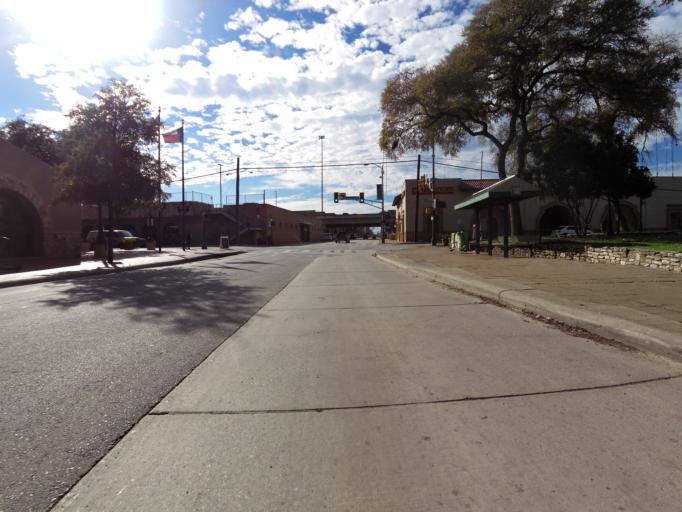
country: US
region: Texas
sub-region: Bexar County
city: San Antonio
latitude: 29.4257
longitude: -98.4998
